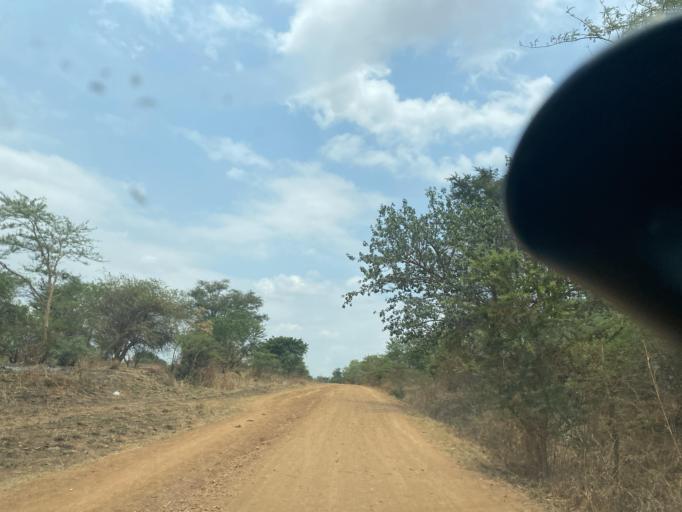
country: ZM
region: Lusaka
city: Chongwe
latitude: -15.5119
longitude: 28.8186
